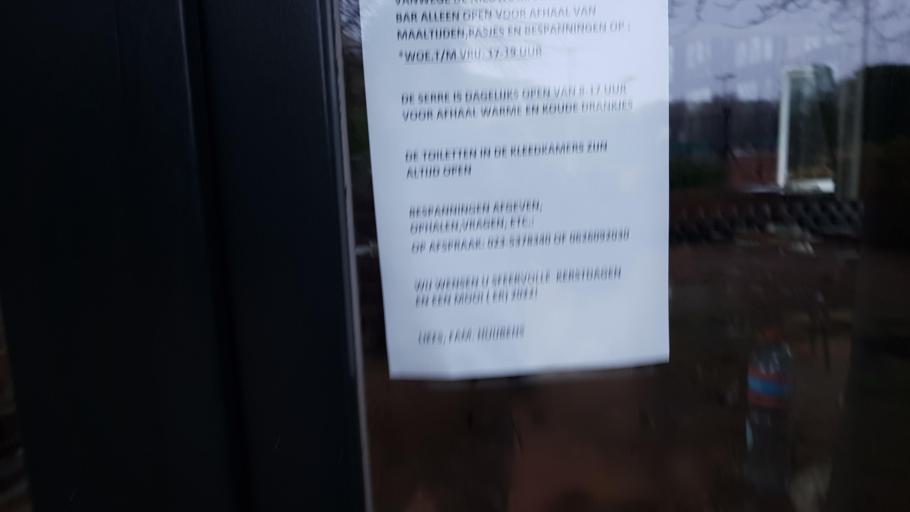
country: NL
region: North Holland
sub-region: Gemeente Bloemendaal
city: Bloemendaal
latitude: 52.4249
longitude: 4.6248
